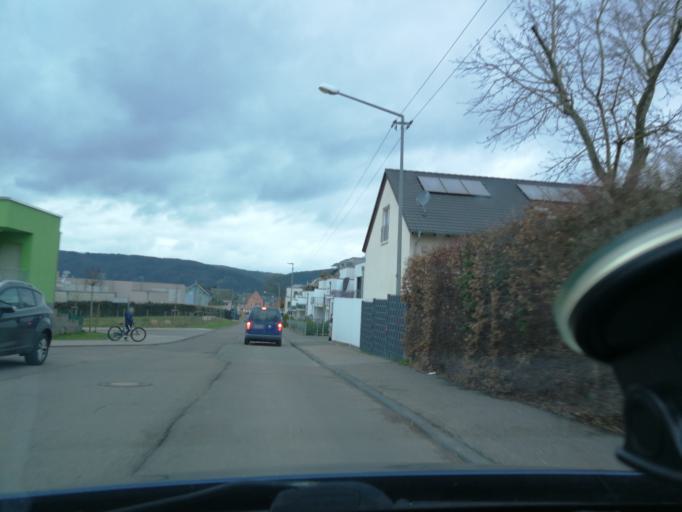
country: DE
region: Rheinland-Pfalz
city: Trier
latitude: 49.7266
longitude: 6.6344
